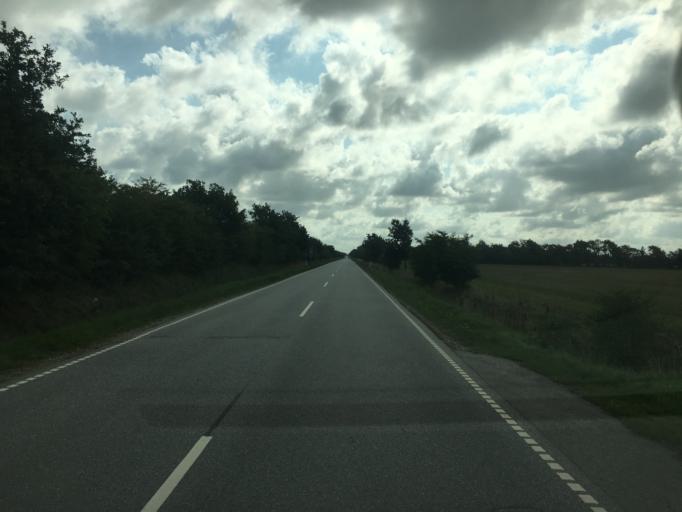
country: DK
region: South Denmark
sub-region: Tonder Kommune
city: Sherrebek
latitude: 55.1252
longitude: 8.8153
